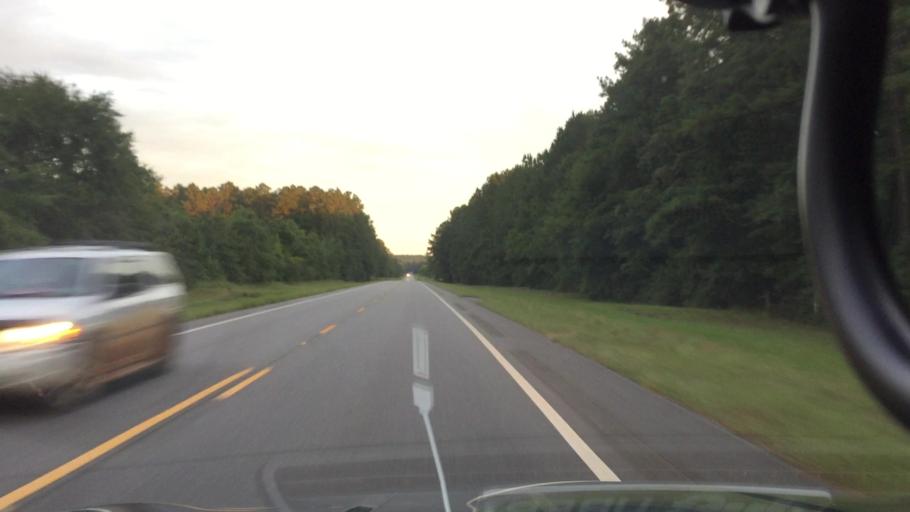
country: US
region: Alabama
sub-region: Coffee County
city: New Brockton
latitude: 31.4865
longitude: -85.9125
